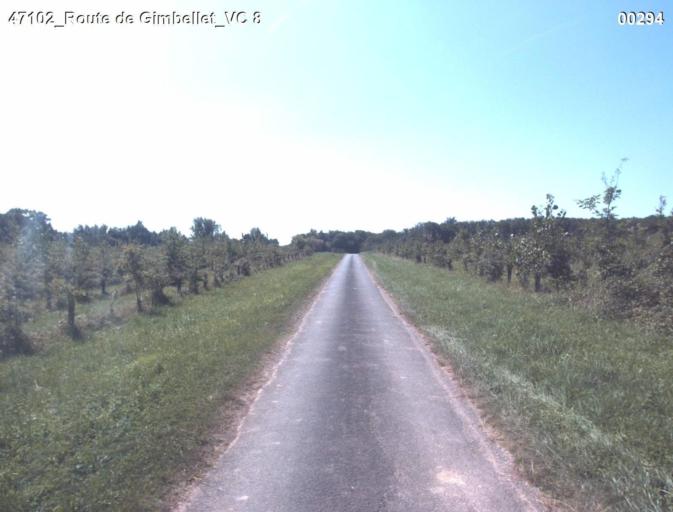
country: FR
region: Aquitaine
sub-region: Departement du Lot-et-Garonne
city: Laplume
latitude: 44.0495
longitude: 0.4468
